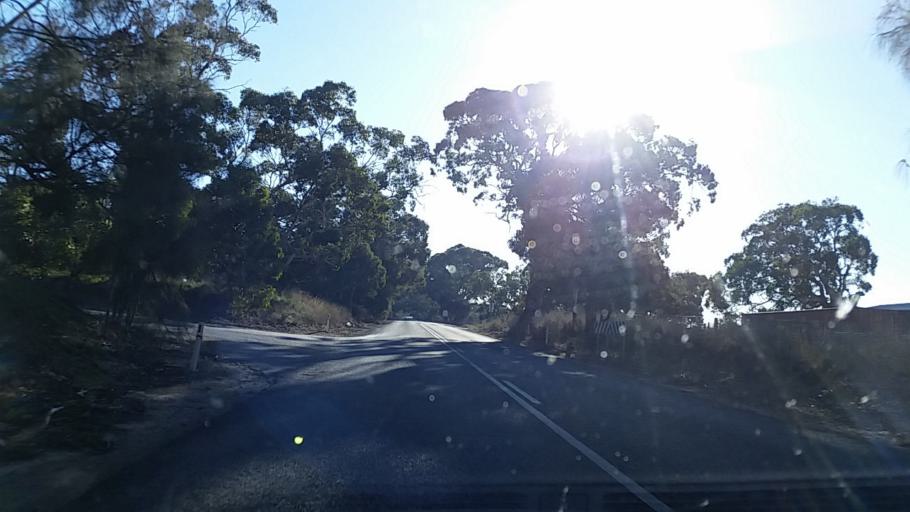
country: AU
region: South Australia
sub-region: Mount Barker
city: Macclesfield
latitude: -35.1473
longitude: 138.9307
